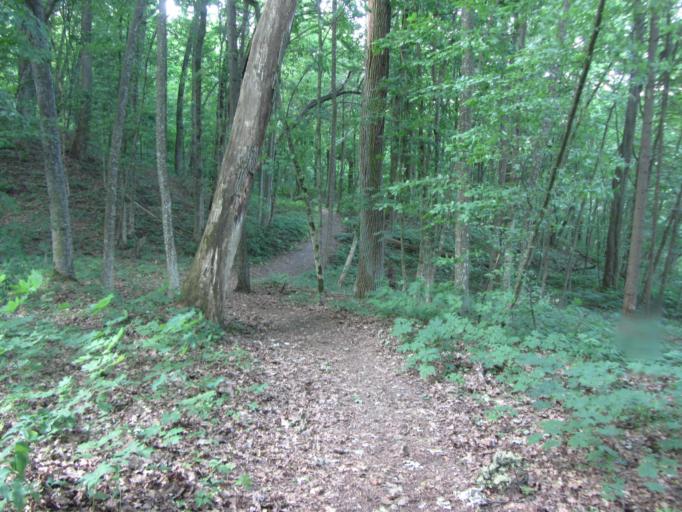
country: LT
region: Alytaus apskritis
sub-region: Alytus
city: Alytus
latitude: 54.3773
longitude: 24.0069
